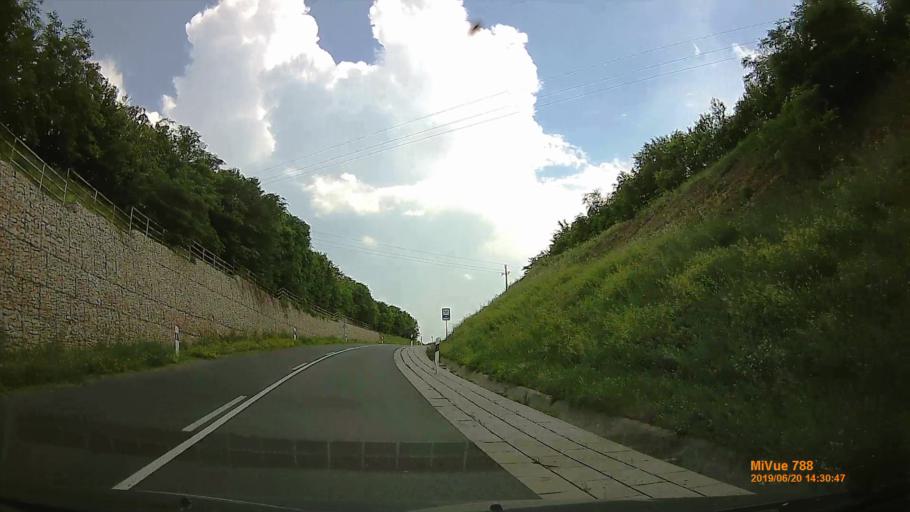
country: HU
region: Baranya
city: Hosszuheteny
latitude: 46.1458
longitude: 18.3481
